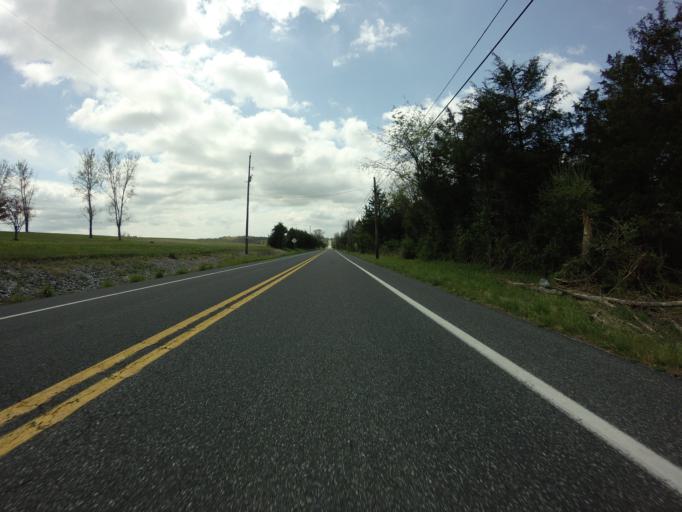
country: US
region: Maryland
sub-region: Frederick County
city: Emmitsburg
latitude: 39.7337
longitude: -77.2933
